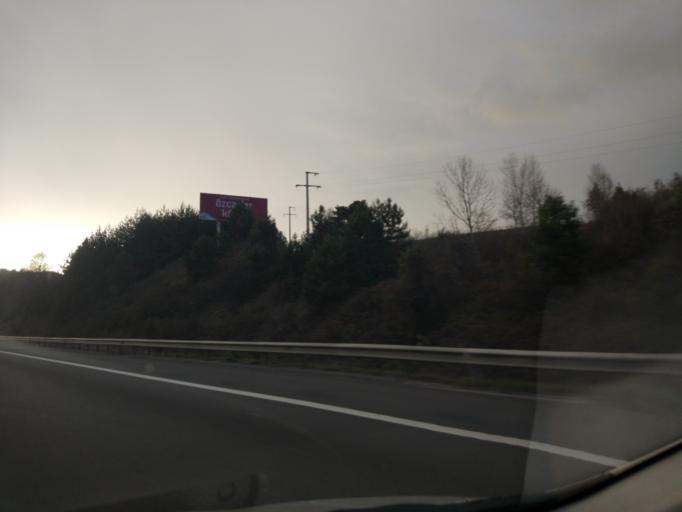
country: TR
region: Bolu
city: Bolu
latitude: 40.7369
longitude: 31.8174
